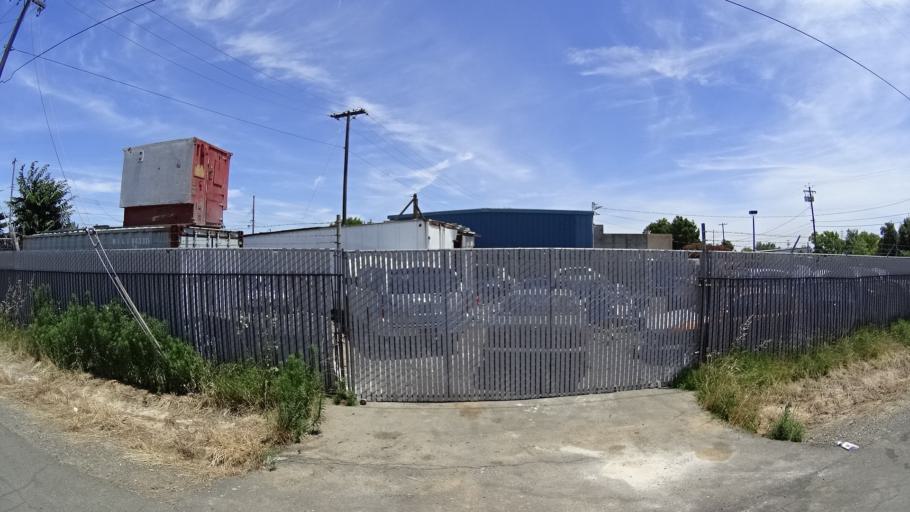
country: US
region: California
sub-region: Sacramento County
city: Florin
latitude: 38.5369
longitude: -121.4117
